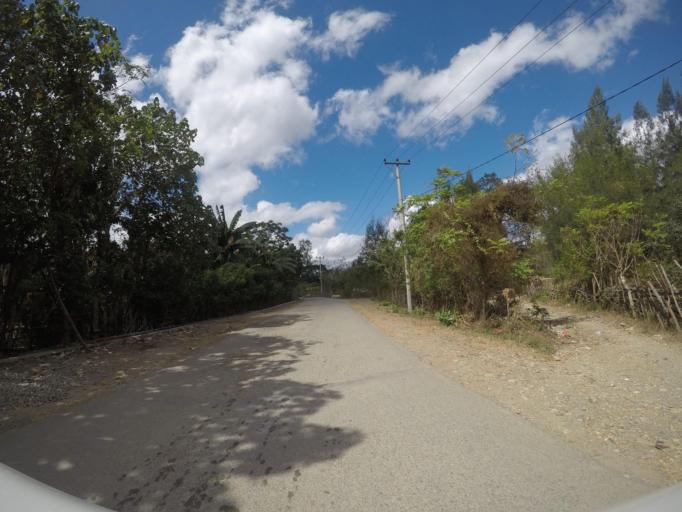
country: TL
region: Lautem
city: Lospalos
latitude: -8.4543
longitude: 126.8218
